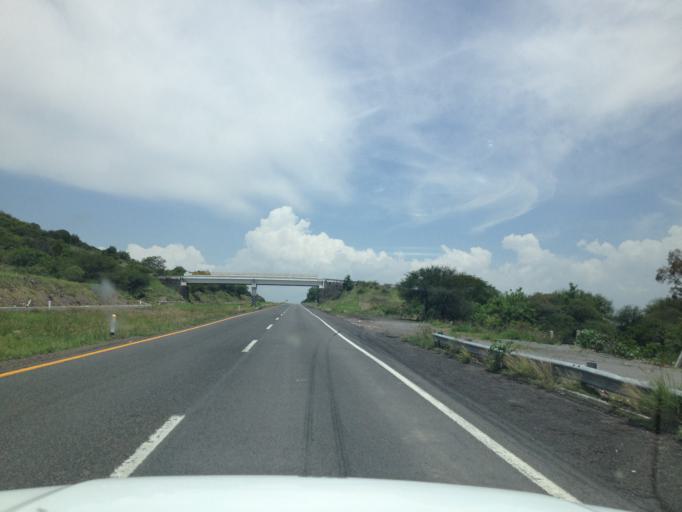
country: MX
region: Michoacan
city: Copandaro de Galeana
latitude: 19.9000
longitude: -101.2626
